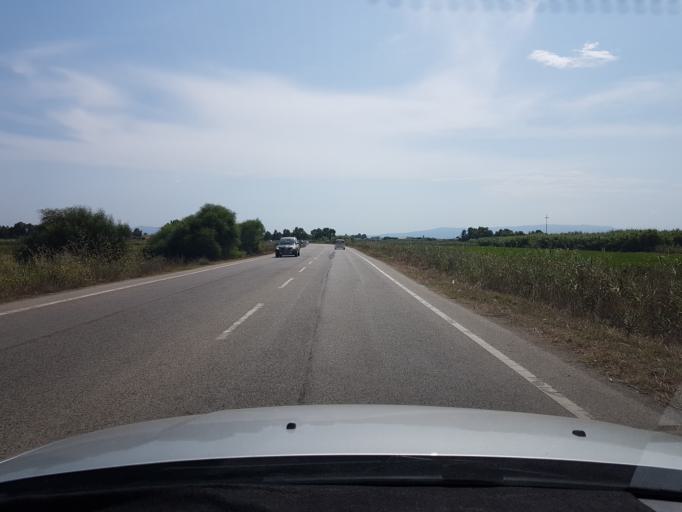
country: IT
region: Sardinia
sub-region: Provincia di Oristano
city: Cabras
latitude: 39.9183
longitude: 8.5265
